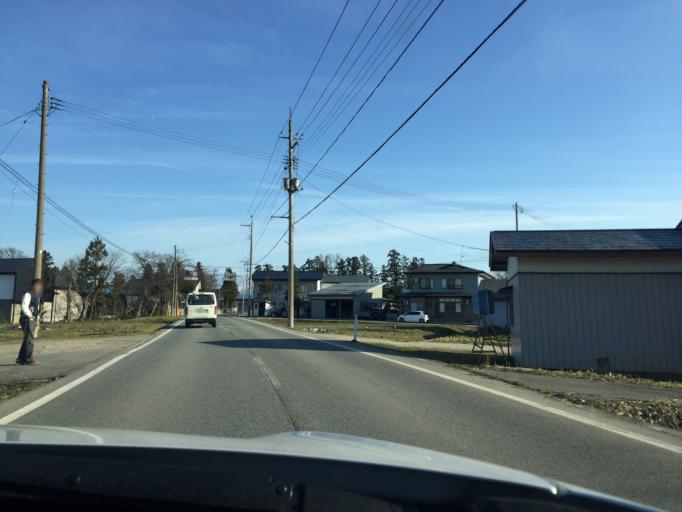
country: JP
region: Yamagata
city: Yonezawa
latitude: 37.9816
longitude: 140.0622
